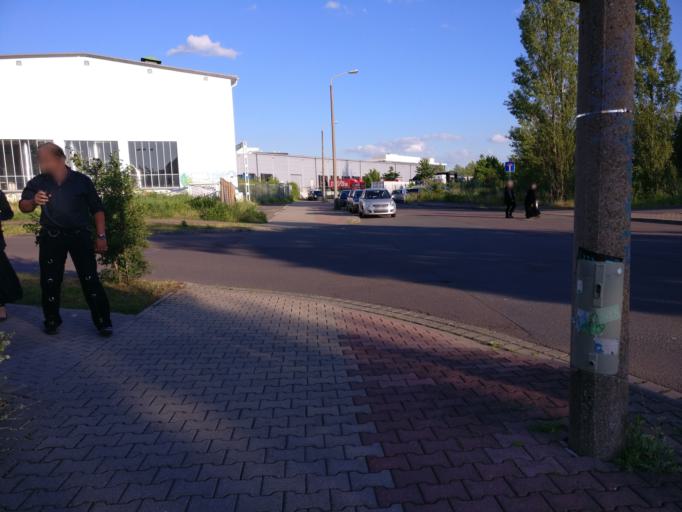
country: DE
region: Saxony
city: Leipzig
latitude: 51.3185
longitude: 12.3927
